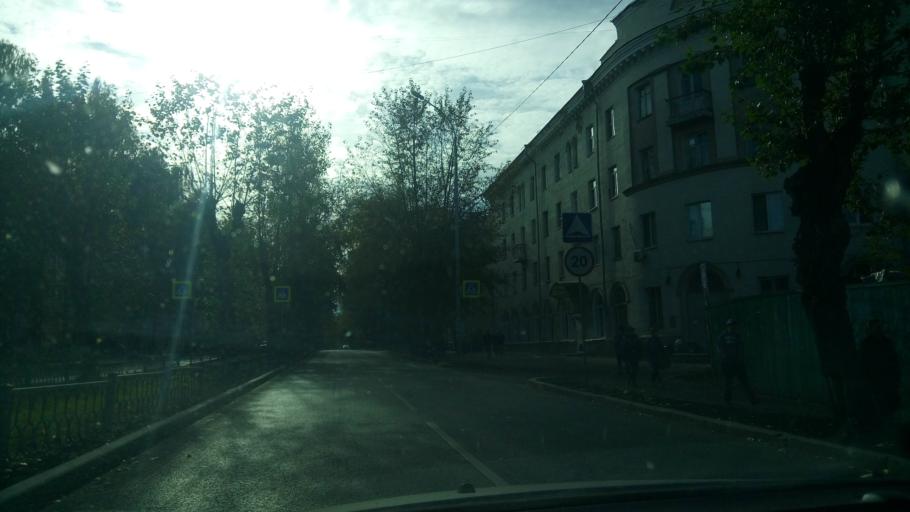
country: RU
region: Sverdlovsk
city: Yekaterinburg
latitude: 56.8890
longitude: 60.6194
